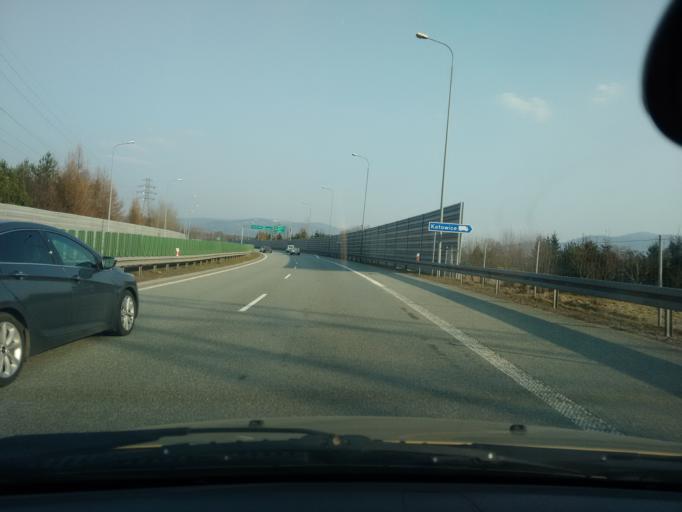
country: PL
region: Silesian Voivodeship
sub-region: Powiat cieszynski
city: Skoczow
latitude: 49.7851
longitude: 18.7951
